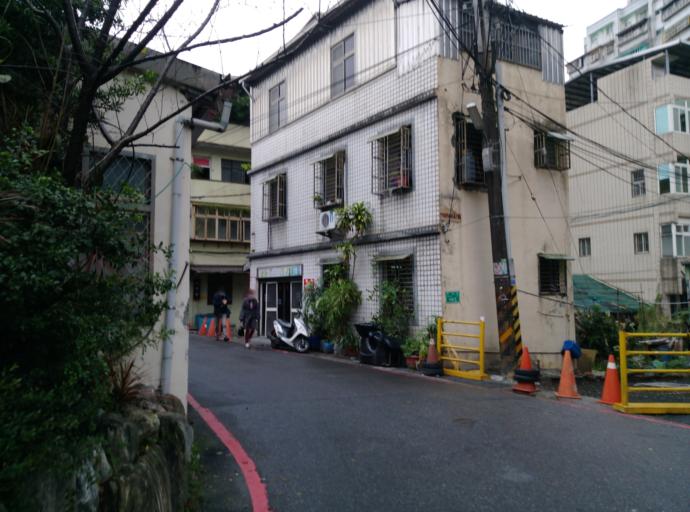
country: TW
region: Taiwan
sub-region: Keelung
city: Keelung
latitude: 25.1247
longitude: 121.7421
